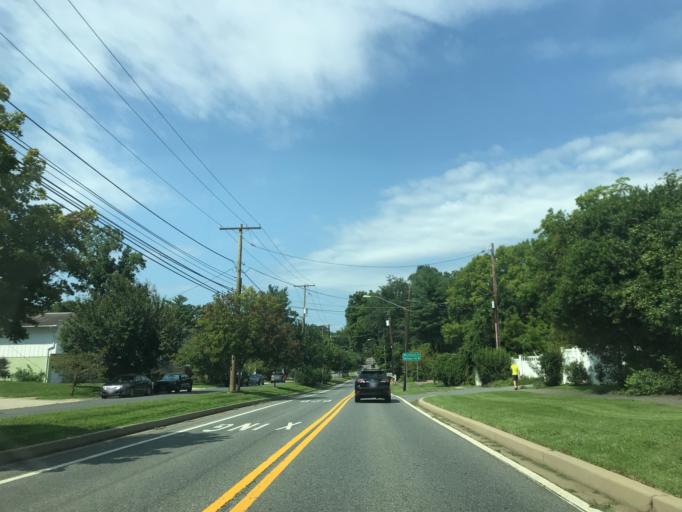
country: US
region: Maryland
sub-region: Montgomery County
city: Bethesda
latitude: 38.9878
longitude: -77.1294
